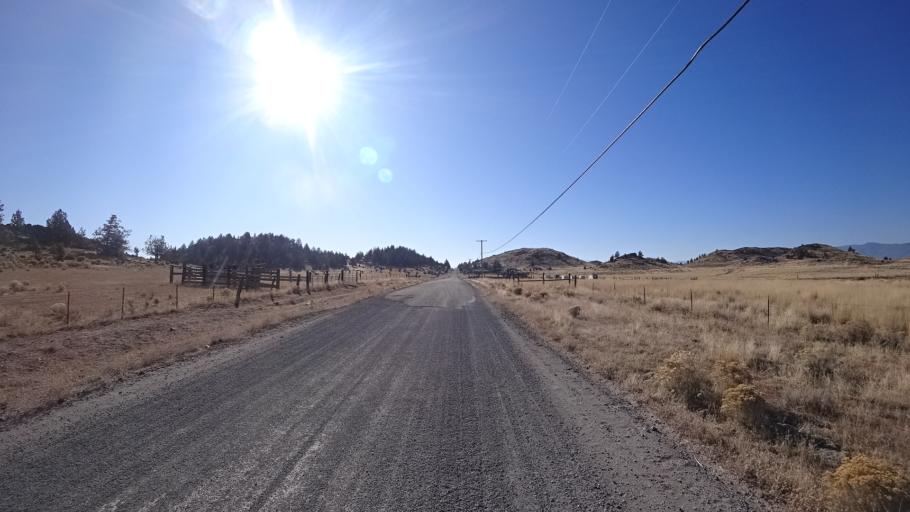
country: US
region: California
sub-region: Siskiyou County
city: Montague
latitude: 41.7033
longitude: -122.4377
